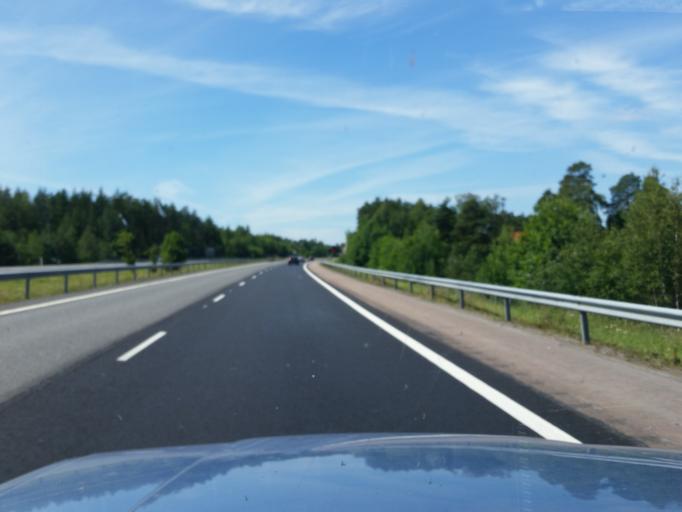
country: FI
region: Varsinais-Suomi
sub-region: Turku
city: Kaarina
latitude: 60.4257
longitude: 22.4299
